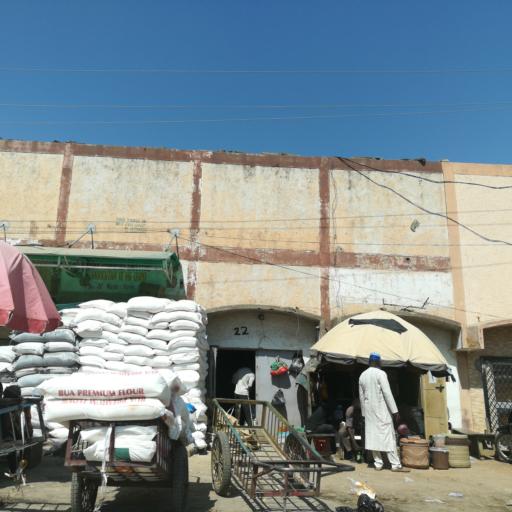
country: NG
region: Kano
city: Kano
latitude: 12.0069
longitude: 8.5390
